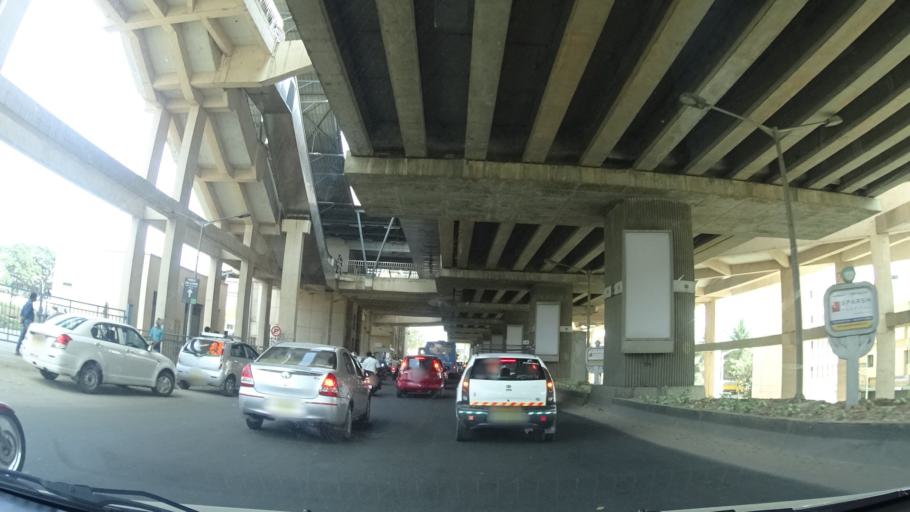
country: IN
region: Karnataka
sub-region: Bangalore Urban
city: Bangalore
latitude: 13.0236
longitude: 77.5495
